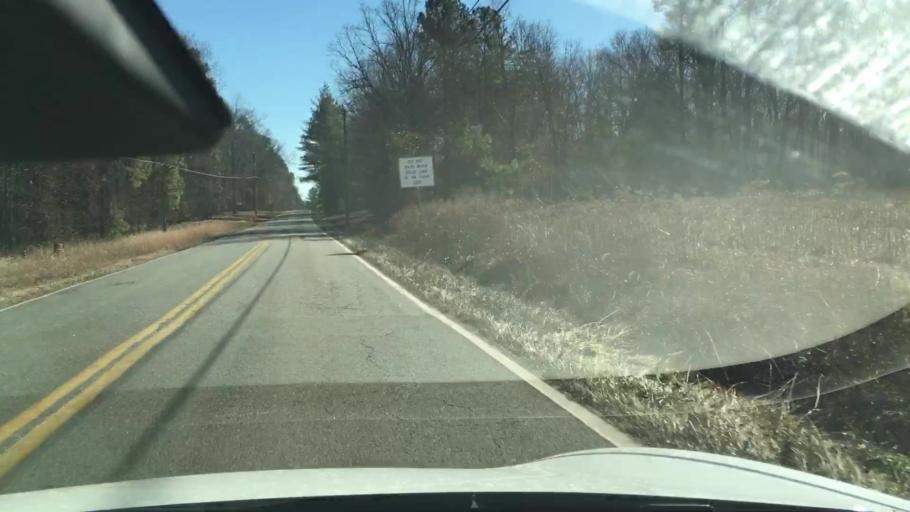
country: US
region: Virginia
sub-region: Henrico County
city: Short Pump
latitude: 37.5749
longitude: -77.7210
